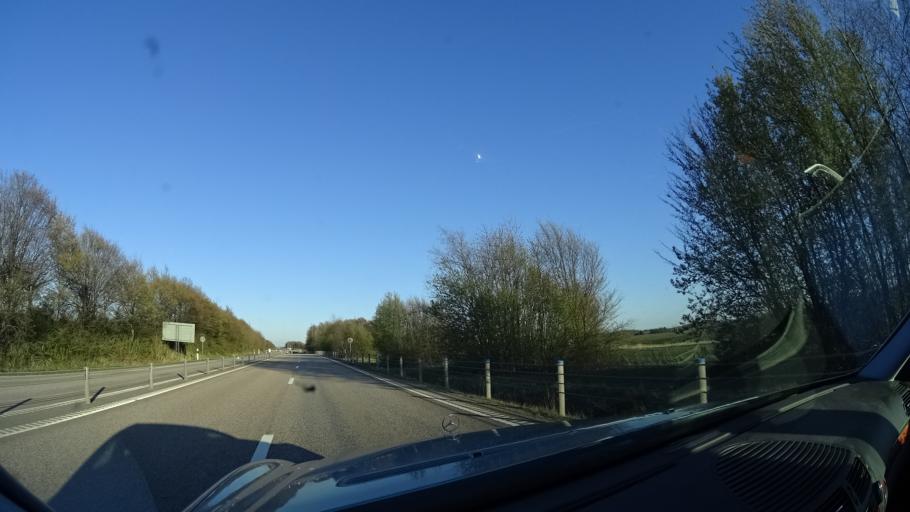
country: SE
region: Skane
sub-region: Bjuvs Kommun
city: Bjuv
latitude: 56.0794
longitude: 12.8939
